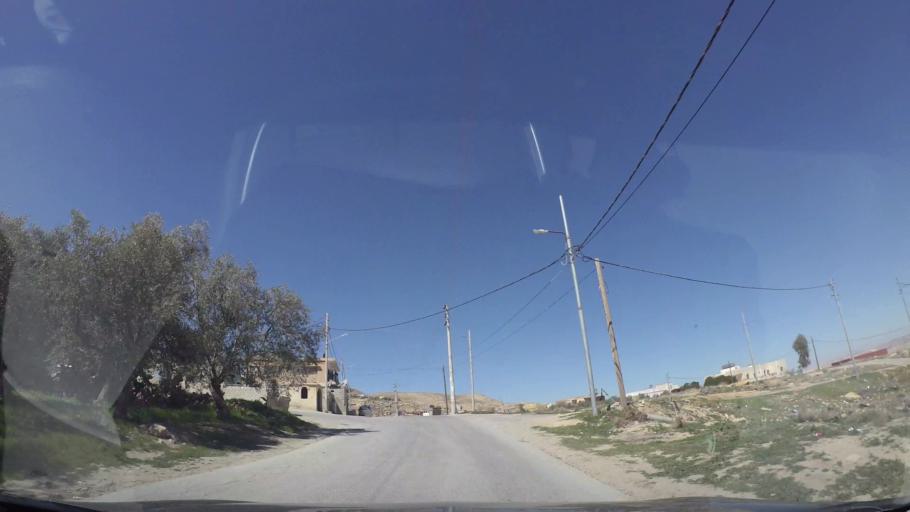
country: JO
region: Tafielah
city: At Tafilah
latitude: 30.8203
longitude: 35.5835
